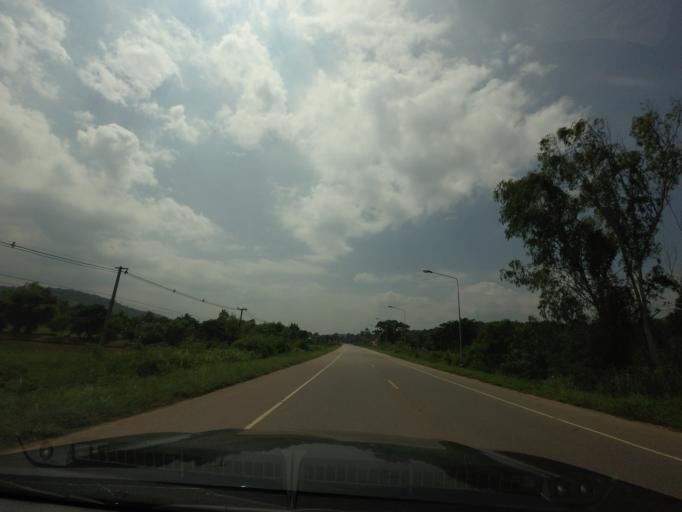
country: TH
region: Loei
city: Phu Ruea
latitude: 17.4472
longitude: 101.3396
